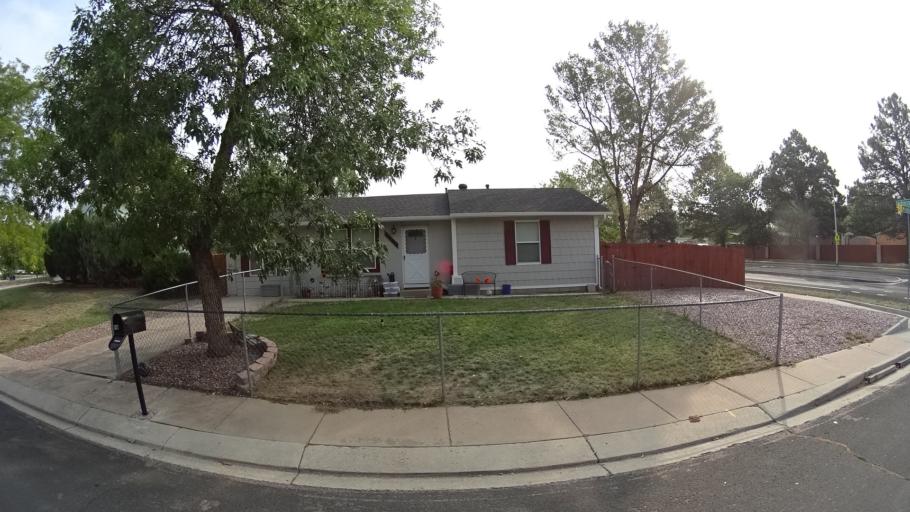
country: US
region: Colorado
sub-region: El Paso County
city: Stratmoor
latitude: 38.7983
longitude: -104.7398
